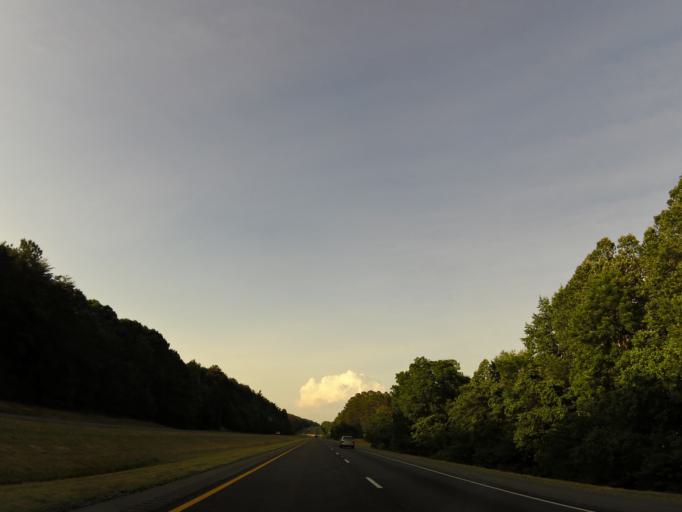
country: US
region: Alabama
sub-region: DeKalb County
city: Henagar
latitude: 34.5607
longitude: -85.6694
